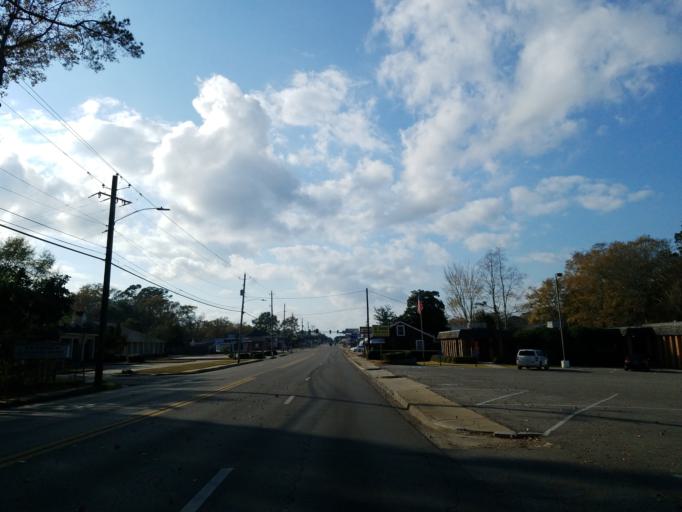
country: US
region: Mississippi
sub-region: Forrest County
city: Hattiesburg
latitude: 31.3248
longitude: -89.3021
